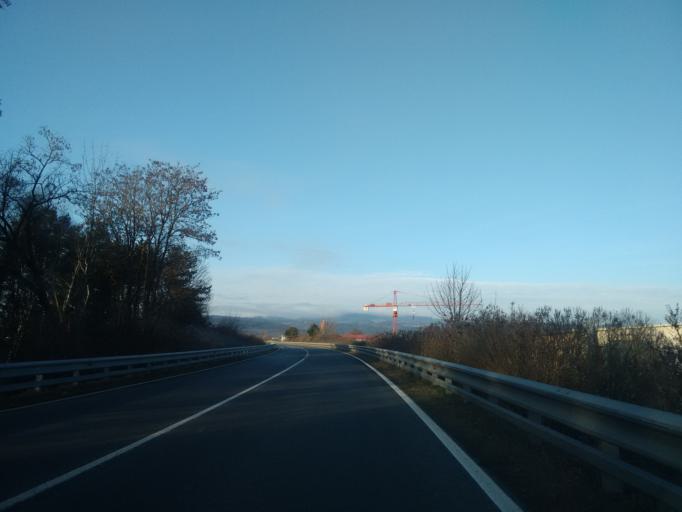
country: AT
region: Lower Austria
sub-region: Politischer Bezirk Melk
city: Melk
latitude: 48.2258
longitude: 15.3504
